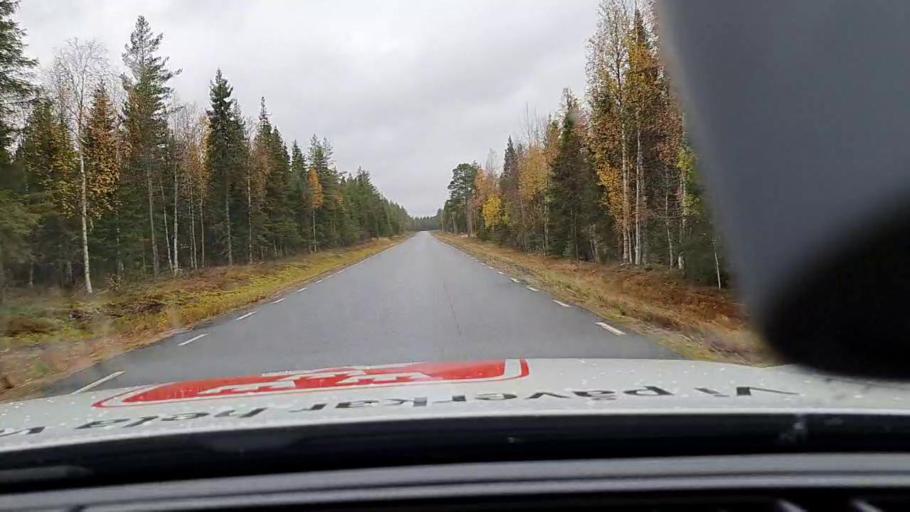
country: SE
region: Norrbotten
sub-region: Haparanda Kommun
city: Haparanda
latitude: 65.9352
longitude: 23.8119
